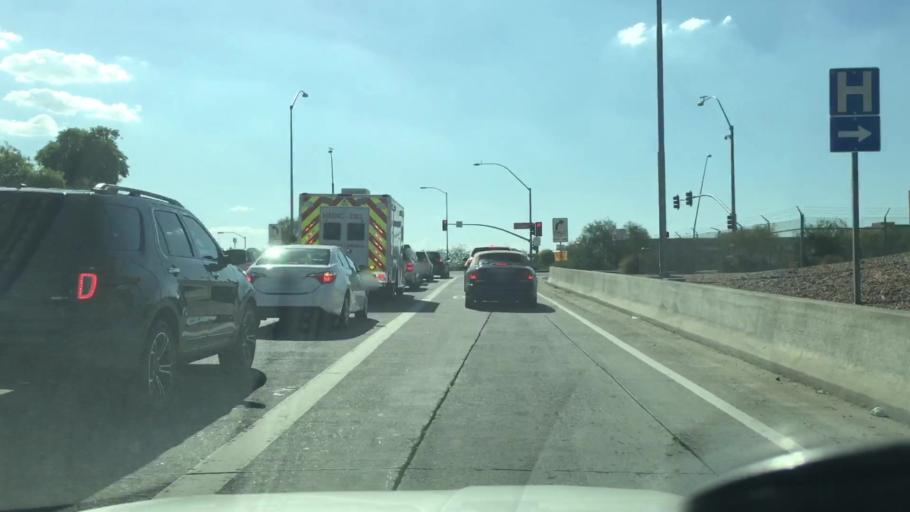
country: US
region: Arizona
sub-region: Maricopa County
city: Tempe
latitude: 33.3864
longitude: -111.8738
